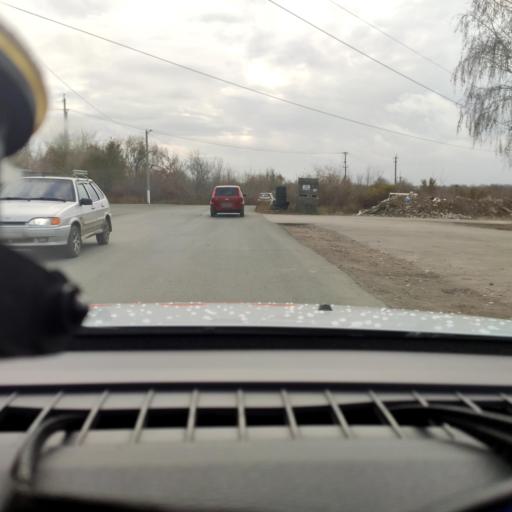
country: RU
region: Samara
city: Chapayevsk
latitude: 52.9932
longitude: 49.7318
